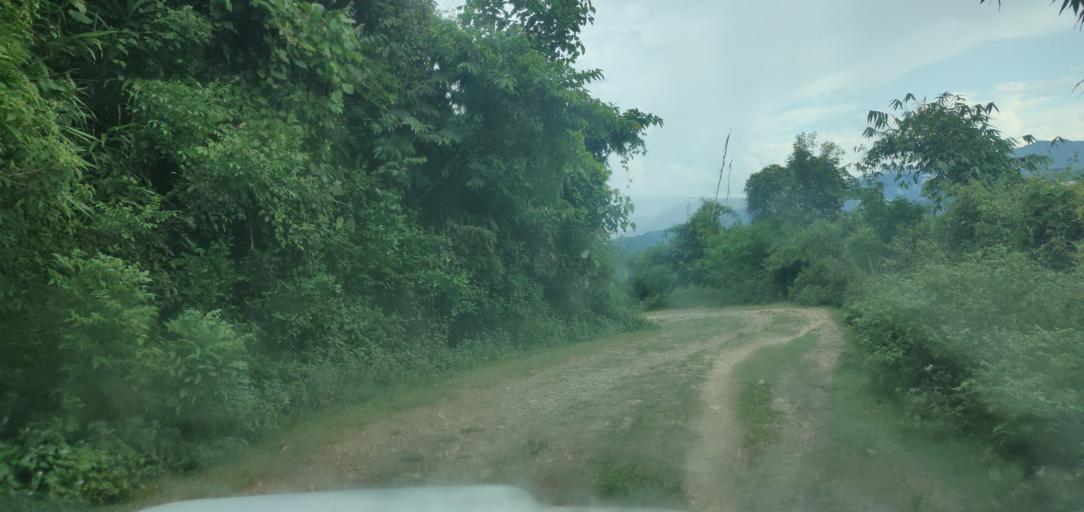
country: LA
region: Phongsali
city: Phongsali
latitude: 21.4470
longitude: 102.3123
